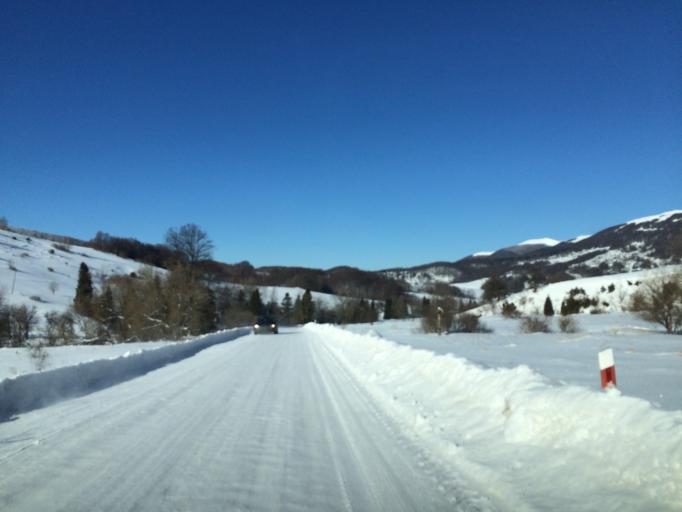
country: PL
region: Subcarpathian Voivodeship
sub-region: Powiat bieszczadzki
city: Lutowiska
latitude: 49.1294
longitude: 22.5827
